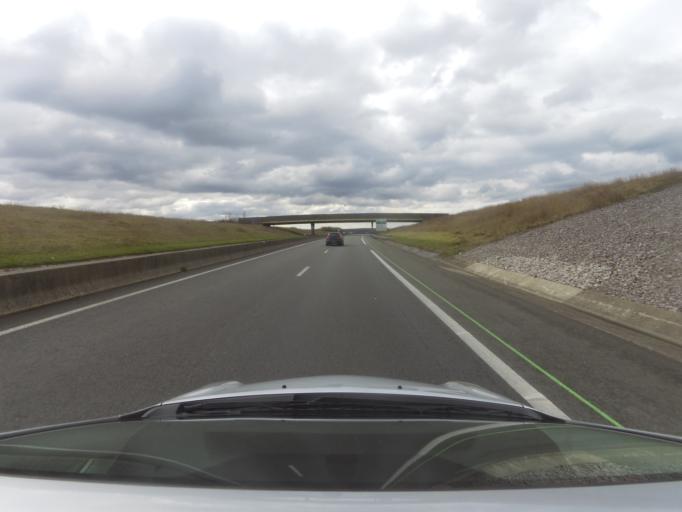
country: FR
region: Nord-Pas-de-Calais
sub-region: Departement du Pas-de-Calais
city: Etaples
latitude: 50.5226
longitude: 1.6871
